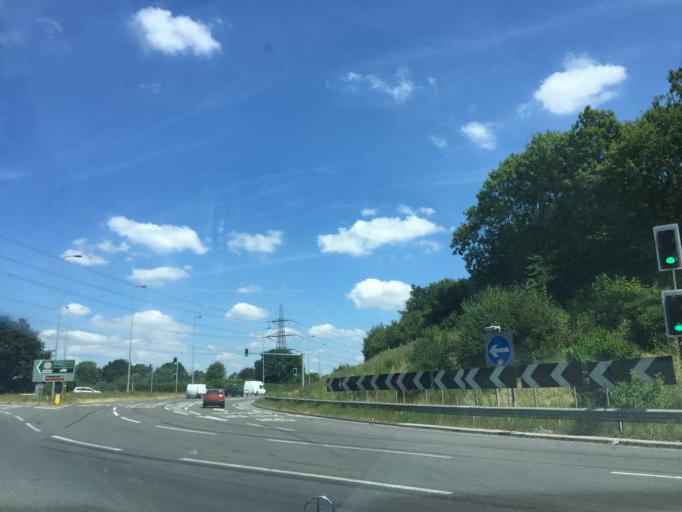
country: GB
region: England
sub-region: Leicestershire
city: Hinckley
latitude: 52.5150
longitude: -1.3634
